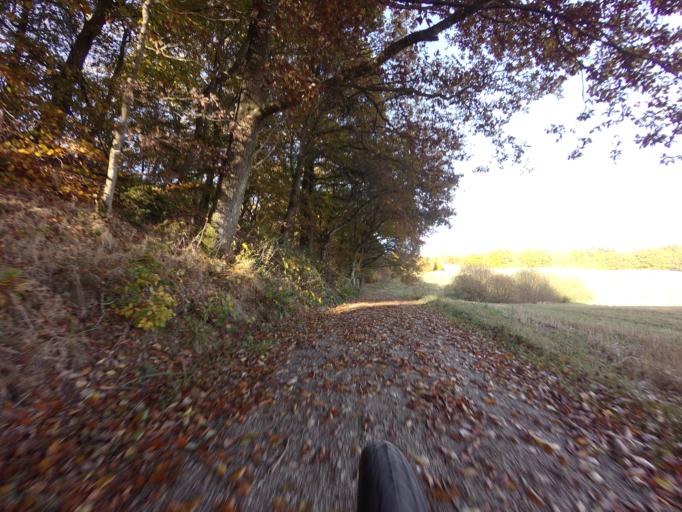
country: DK
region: Central Jutland
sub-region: Syddjurs Kommune
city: Ryomgard
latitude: 56.4468
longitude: 10.6211
